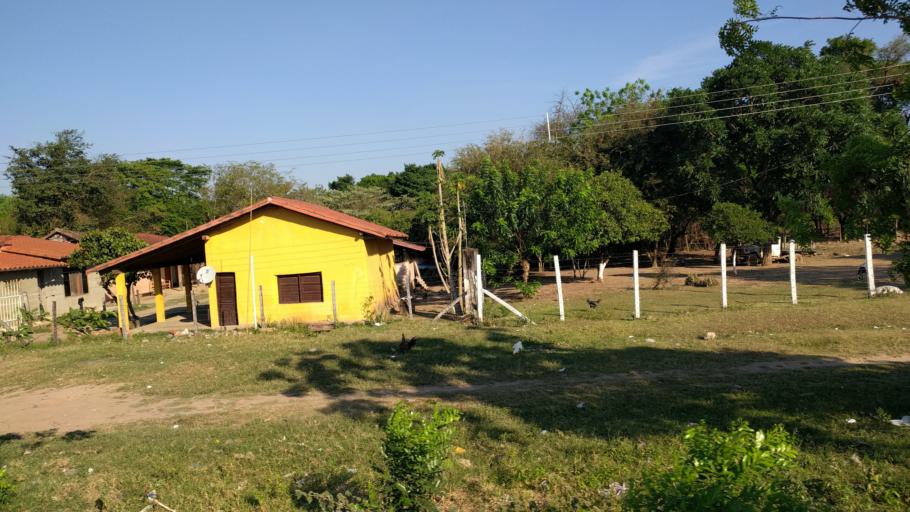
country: BO
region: Santa Cruz
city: Jorochito
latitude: -18.1381
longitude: -63.4764
